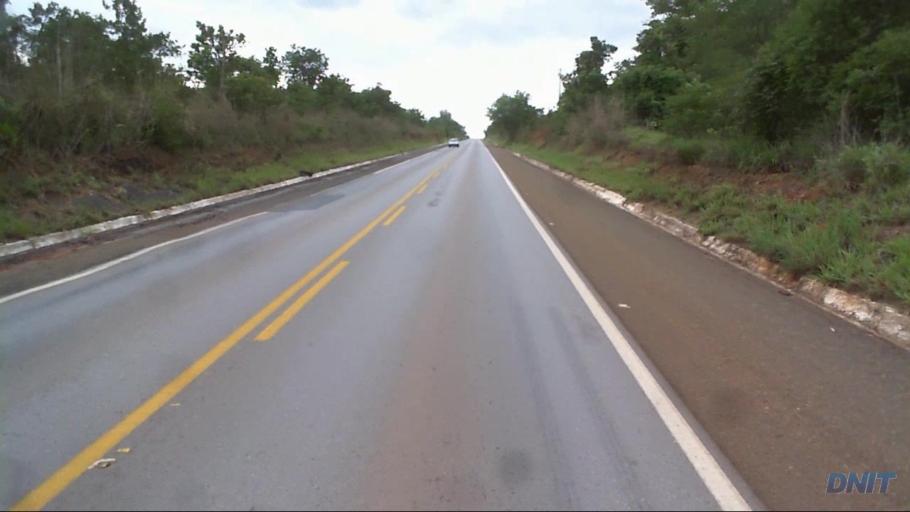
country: BR
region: Goias
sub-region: Uruacu
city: Uruacu
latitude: -14.7539
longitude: -49.0706
